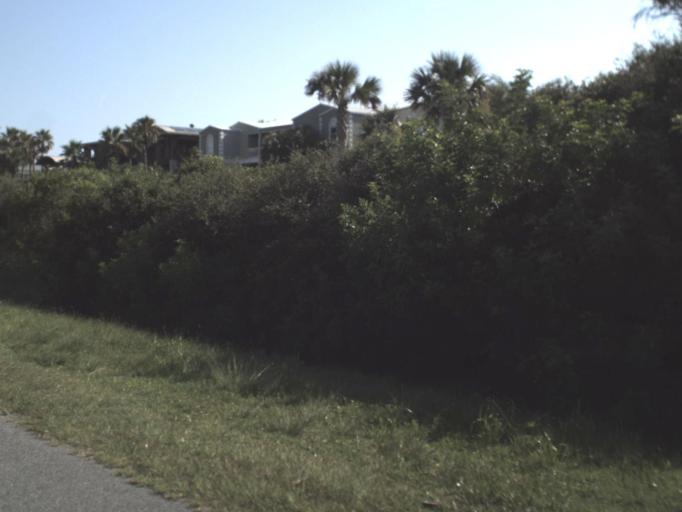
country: US
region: Florida
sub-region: Saint Johns County
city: Butler Beach
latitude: 29.7486
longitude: -81.2459
